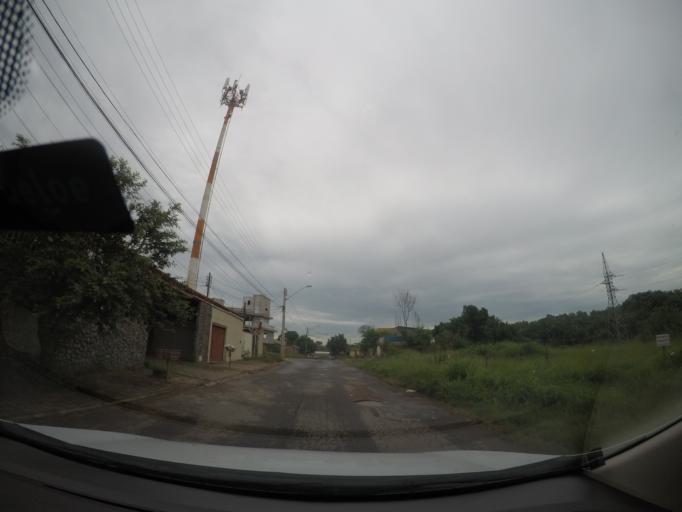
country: BR
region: Goias
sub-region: Goiania
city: Goiania
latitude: -16.6467
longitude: -49.2637
